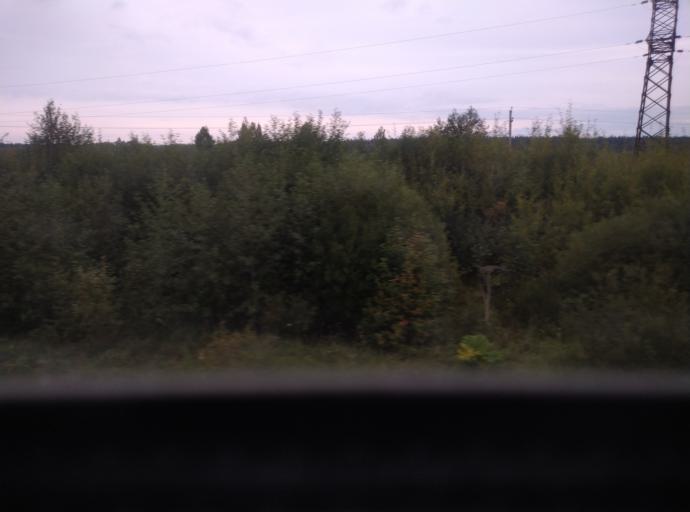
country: RU
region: Jaroslavl
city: Tunoshna
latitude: 57.4880
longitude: 40.1438
